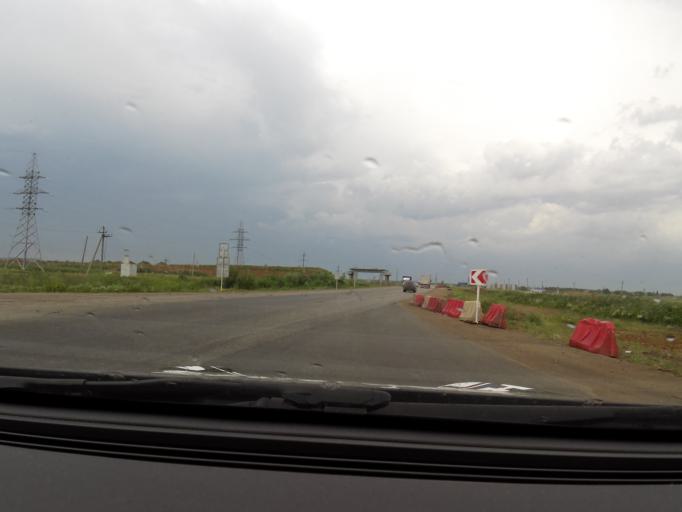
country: RU
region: Bashkortostan
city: Asanovo
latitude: 54.8998
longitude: 55.6325
